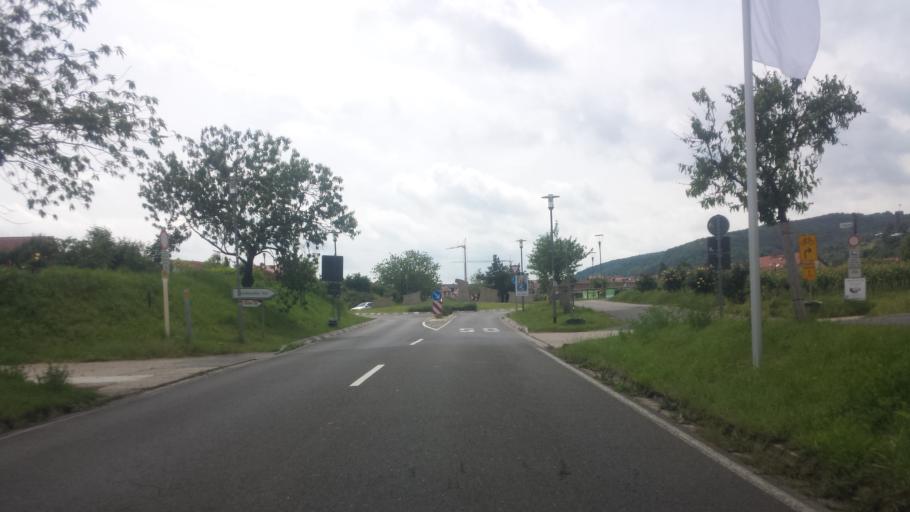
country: DE
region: Rheinland-Pfalz
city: Wachenheim
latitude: 49.4460
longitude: 8.1779
